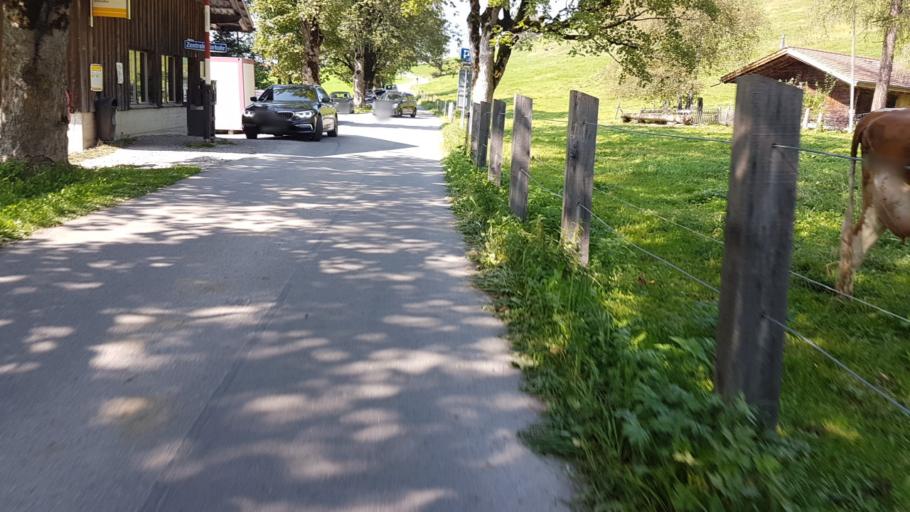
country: CH
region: Bern
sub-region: Frutigen-Niedersimmental District
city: Aeschi
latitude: 46.6369
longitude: 7.7353
